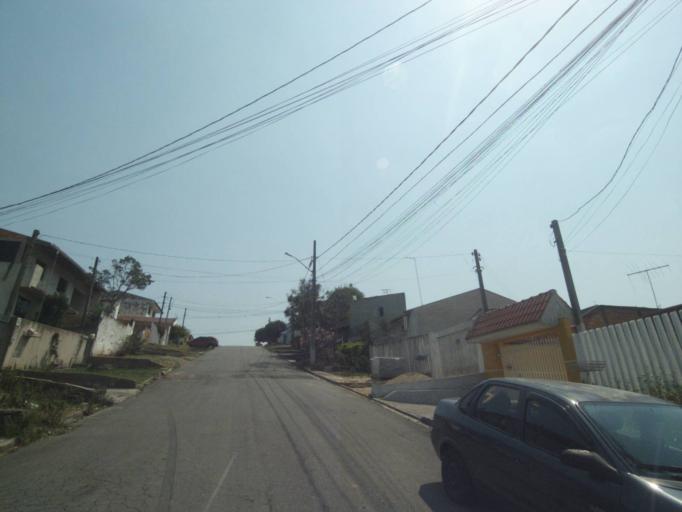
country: BR
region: Parana
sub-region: Sao Jose Dos Pinhais
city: Sao Jose dos Pinhais
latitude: -25.5387
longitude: -49.2464
